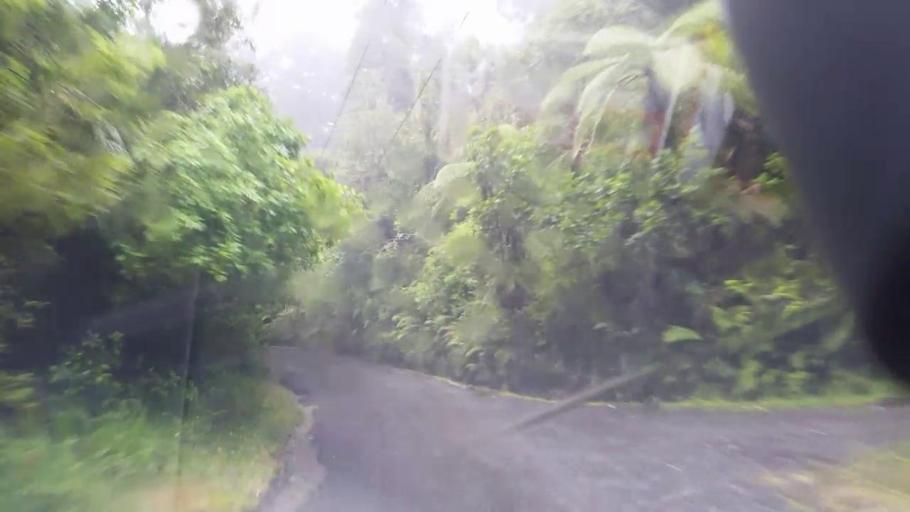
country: NZ
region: Auckland
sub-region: Auckland
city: Titirangi
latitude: -36.9200
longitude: 174.5651
